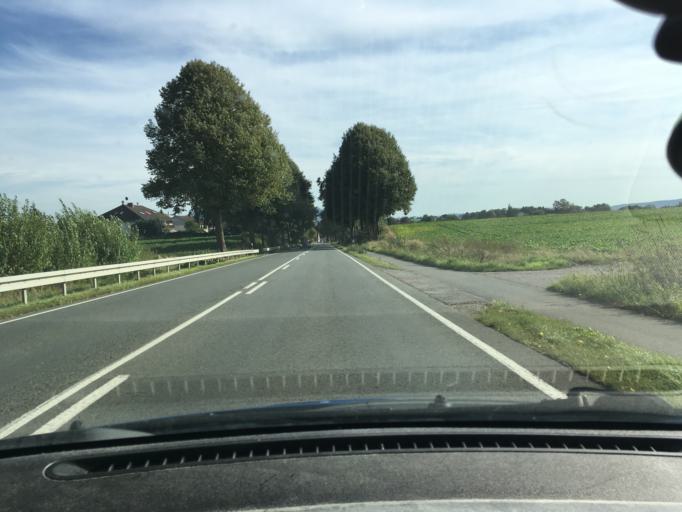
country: DE
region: Lower Saxony
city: Bad Munder am Deister
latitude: 52.1703
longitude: 9.4748
